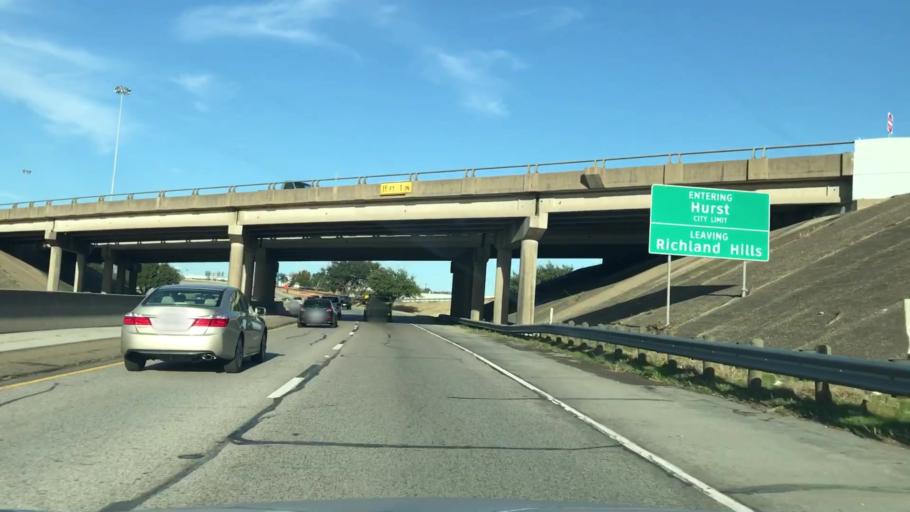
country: US
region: Texas
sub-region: Tarrant County
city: Richland Hills
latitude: 32.8052
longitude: -97.2124
